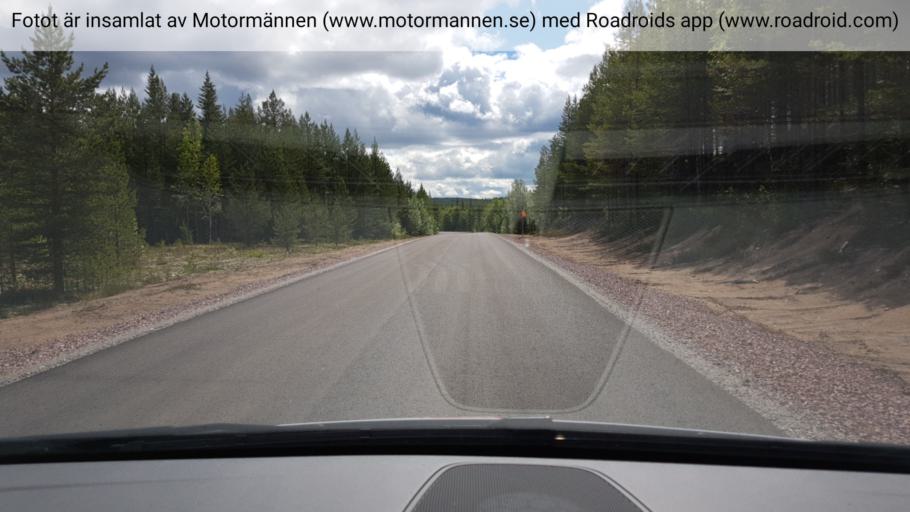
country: SE
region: Jaemtland
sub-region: Harjedalens Kommun
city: Sveg
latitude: 61.6769
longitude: 14.1715
